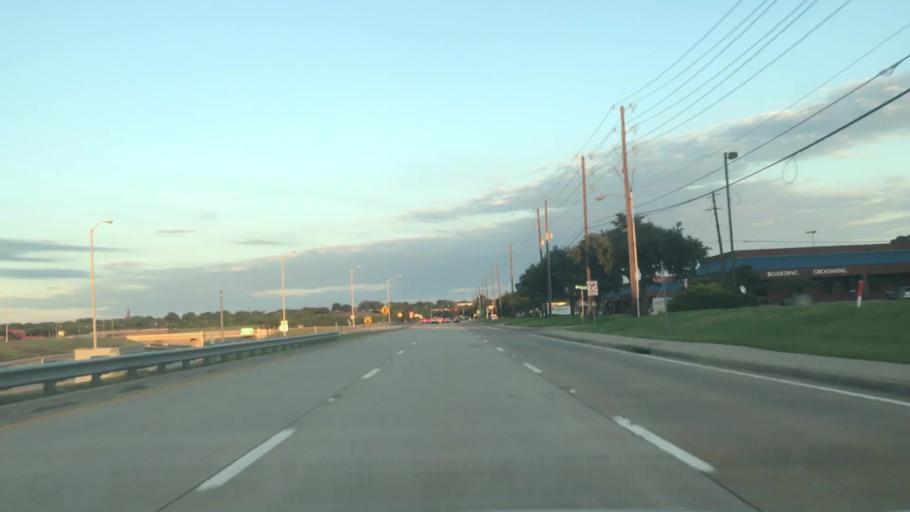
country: US
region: Texas
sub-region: Dallas County
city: Carrollton
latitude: 32.9851
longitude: -96.8737
